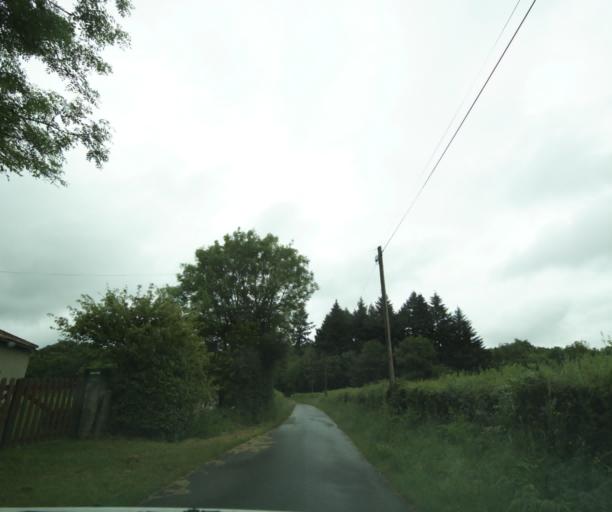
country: FR
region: Bourgogne
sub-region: Departement de Saone-et-Loire
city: Ciry-le-Noble
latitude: 46.5192
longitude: 4.3012
